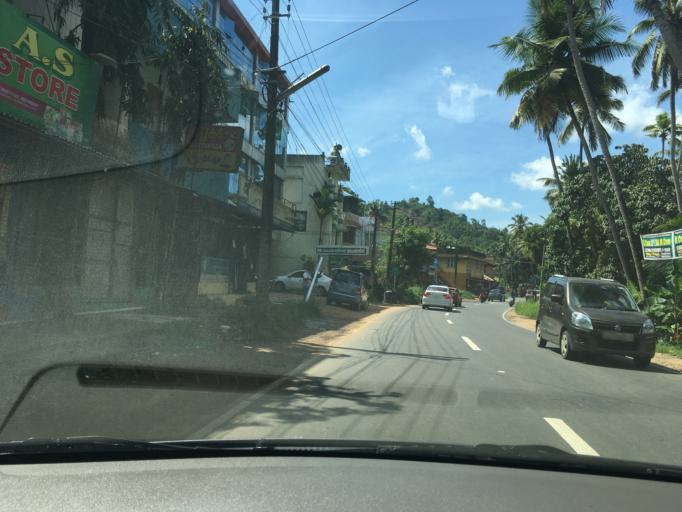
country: IN
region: Kerala
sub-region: Thiruvananthapuram
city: Nedumangad
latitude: 8.5697
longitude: 76.9896
